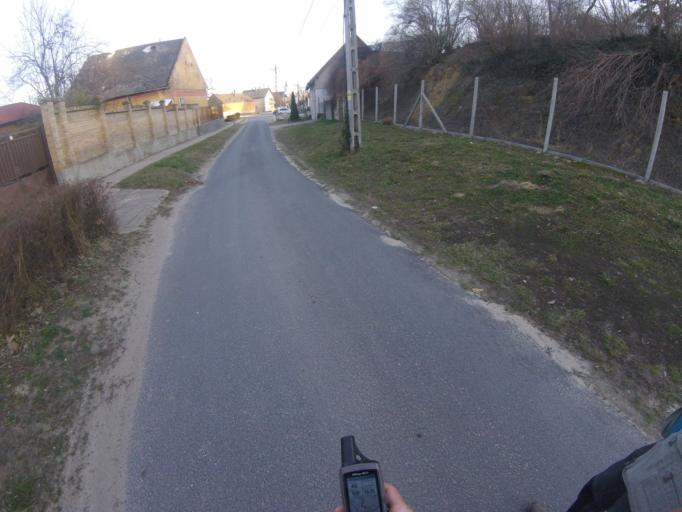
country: HU
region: Tolna
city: Bolcske
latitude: 46.7408
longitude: 18.9650
